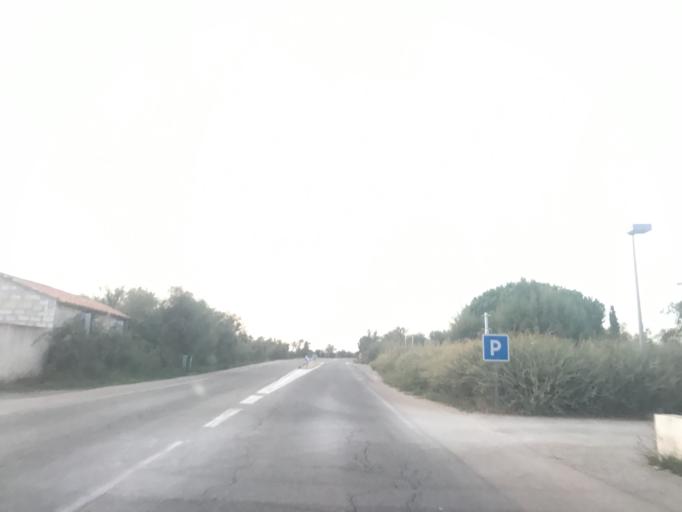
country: FR
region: Provence-Alpes-Cote d'Azur
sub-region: Departement des Bouches-du-Rhone
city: Saintes-Maries-de-la-Mer
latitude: 43.4892
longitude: 4.4038
